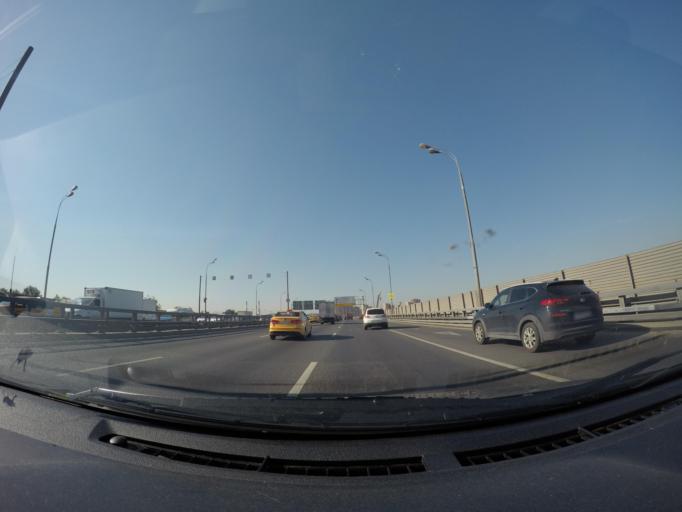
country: RU
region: Moscow
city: Lefortovo
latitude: 55.7454
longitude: 37.6985
